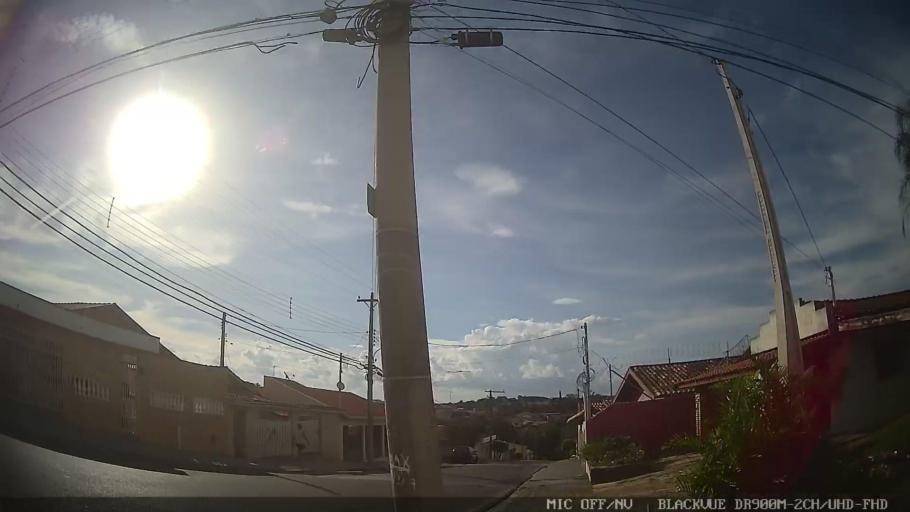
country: BR
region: Sao Paulo
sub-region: Tiete
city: Tiete
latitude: -23.0887
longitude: -47.6959
